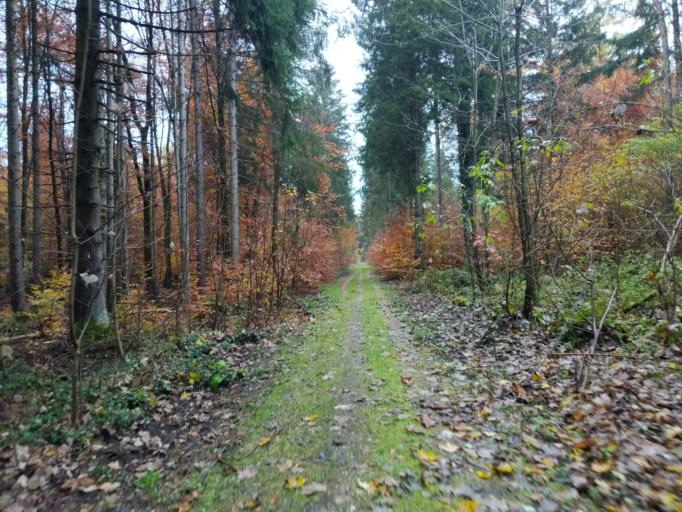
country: DE
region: Bavaria
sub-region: Upper Bavaria
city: Zorneding
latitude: 48.0931
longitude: 11.8467
